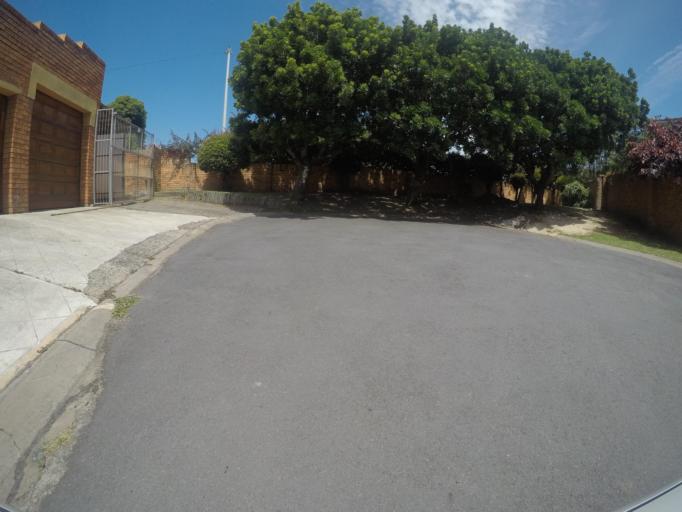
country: ZA
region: Eastern Cape
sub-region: Buffalo City Metropolitan Municipality
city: East London
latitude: -32.9531
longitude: 27.9986
